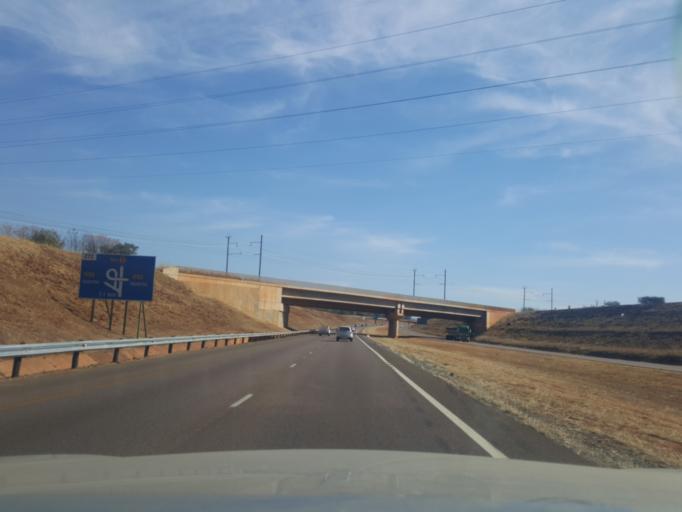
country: ZA
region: Gauteng
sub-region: City of Tshwane Metropolitan Municipality
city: Pretoria
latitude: -25.6493
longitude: 28.1423
